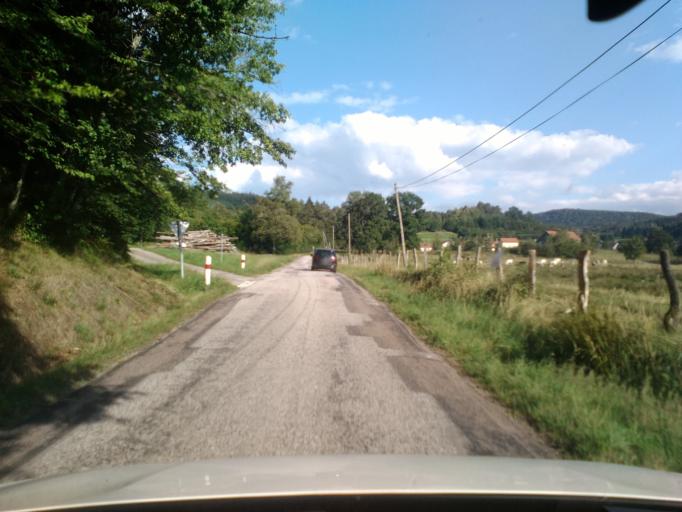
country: FR
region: Lorraine
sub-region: Departement des Vosges
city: Corcieux
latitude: 48.1563
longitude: 6.9155
